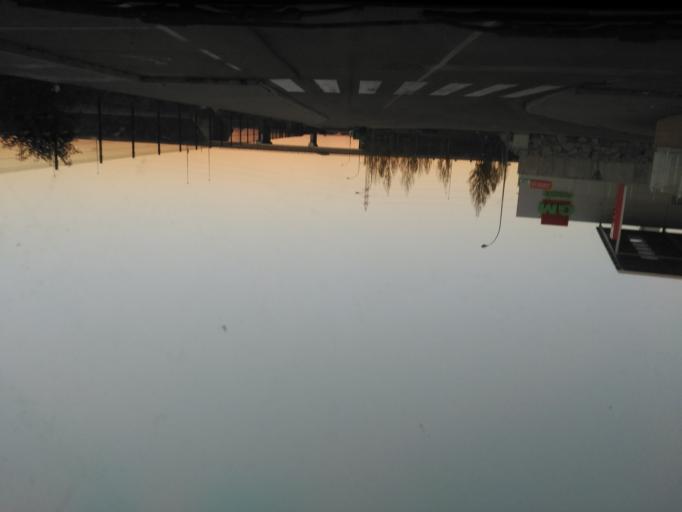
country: ES
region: Castille and Leon
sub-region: Provincia de Salamanca
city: Carbajosa de la Sagrada
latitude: 40.9412
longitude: -5.6517
